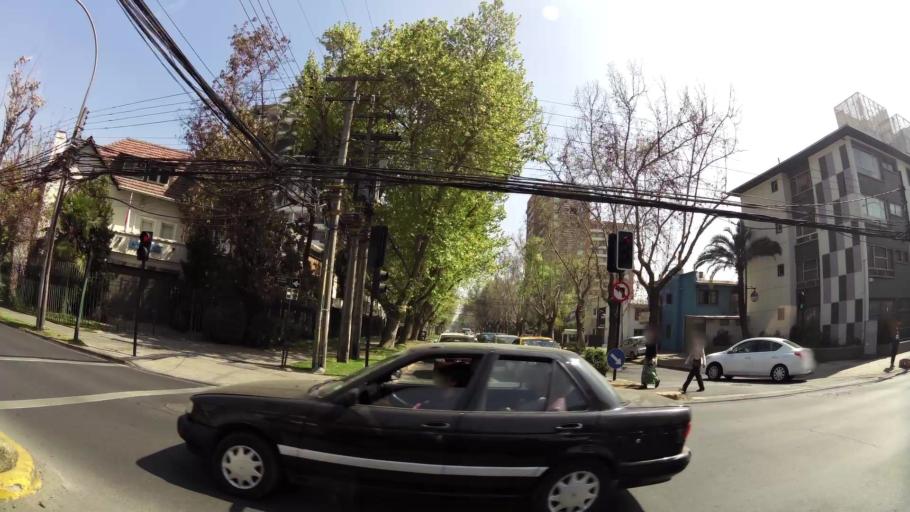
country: CL
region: Santiago Metropolitan
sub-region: Provincia de Santiago
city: Villa Presidente Frei, Nunoa, Santiago, Chile
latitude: -33.4572
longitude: -70.6055
